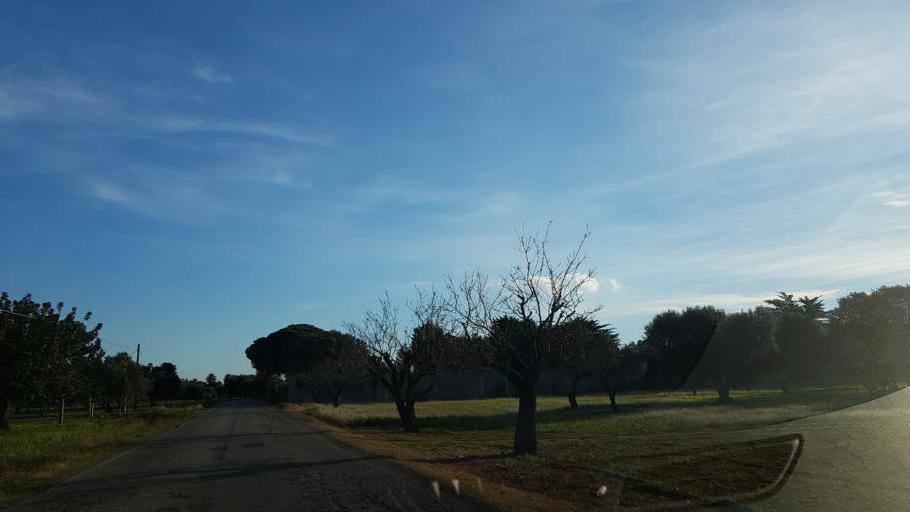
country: IT
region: Apulia
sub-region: Provincia di Brindisi
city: San Vito dei Normanni
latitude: 40.6732
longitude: 17.7767
